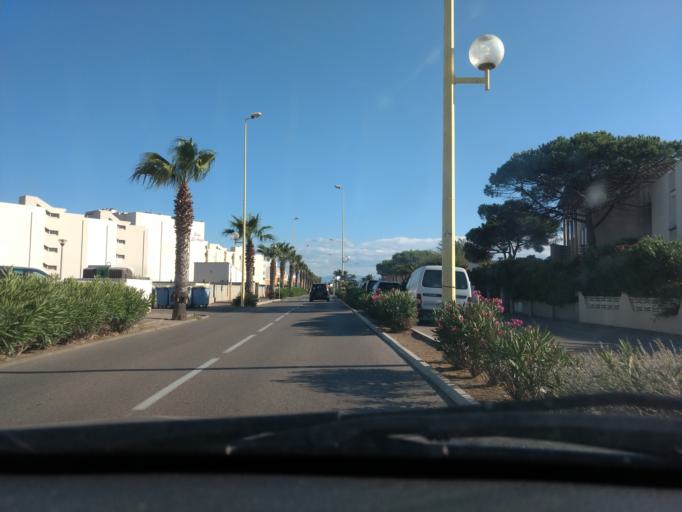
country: FR
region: Languedoc-Roussillon
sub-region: Departement des Pyrenees-Orientales
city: Le Barcares
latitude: 42.8024
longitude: 3.0371
